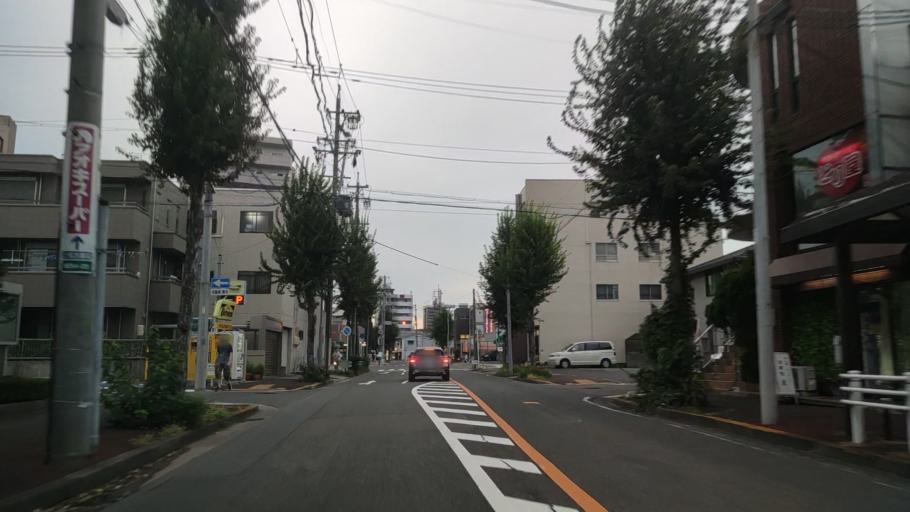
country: JP
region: Aichi
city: Nagoya-shi
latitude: 35.1917
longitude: 136.8956
